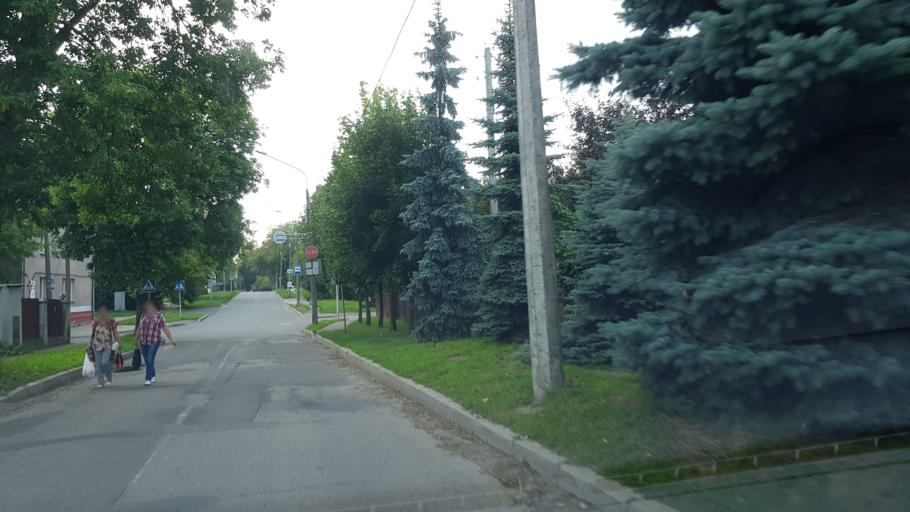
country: BY
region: Minsk
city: Syenitsa
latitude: 53.8697
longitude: 27.5143
